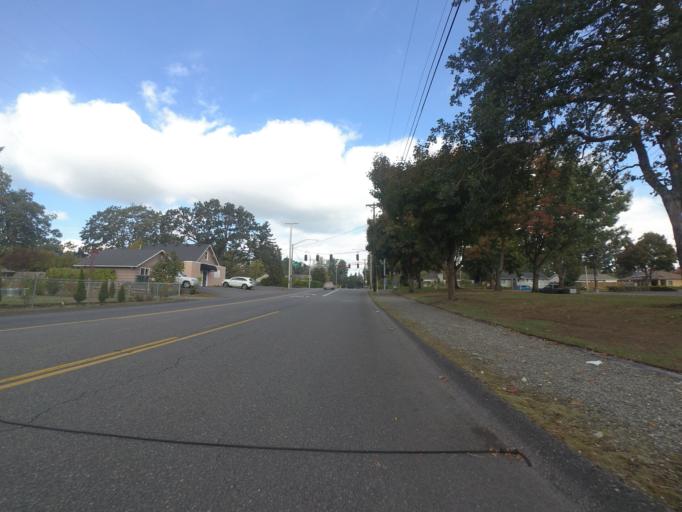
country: US
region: Washington
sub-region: Pierce County
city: Lakewood
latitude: 47.1726
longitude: -122.5218
